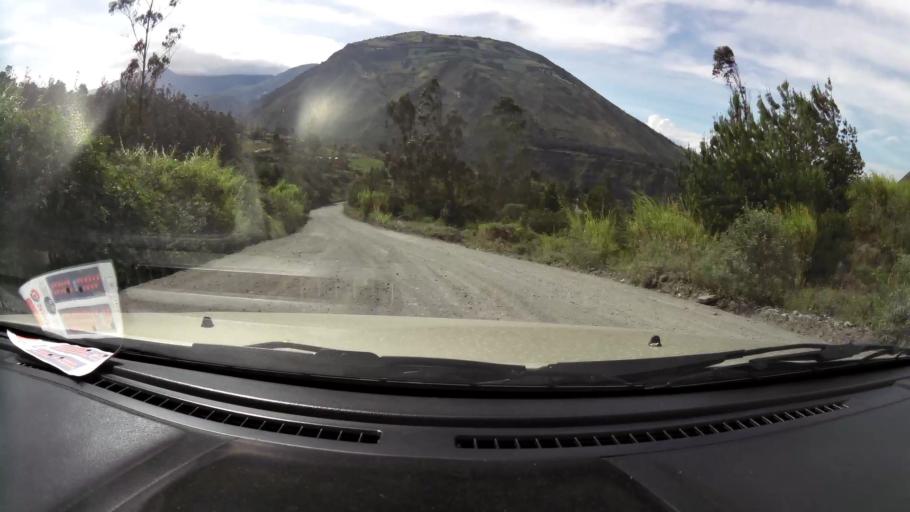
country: EC
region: Tungurahua
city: Banos
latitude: -1.4103
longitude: -78.4698
